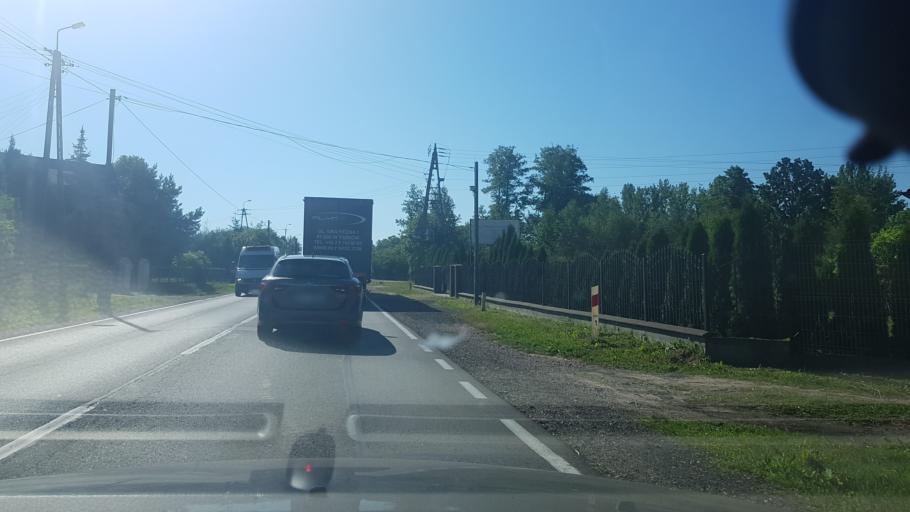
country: PL
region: Masovian Voivodeship
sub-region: Powiat wegrowski
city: Lochow
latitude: 52.5443
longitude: 21.6409
